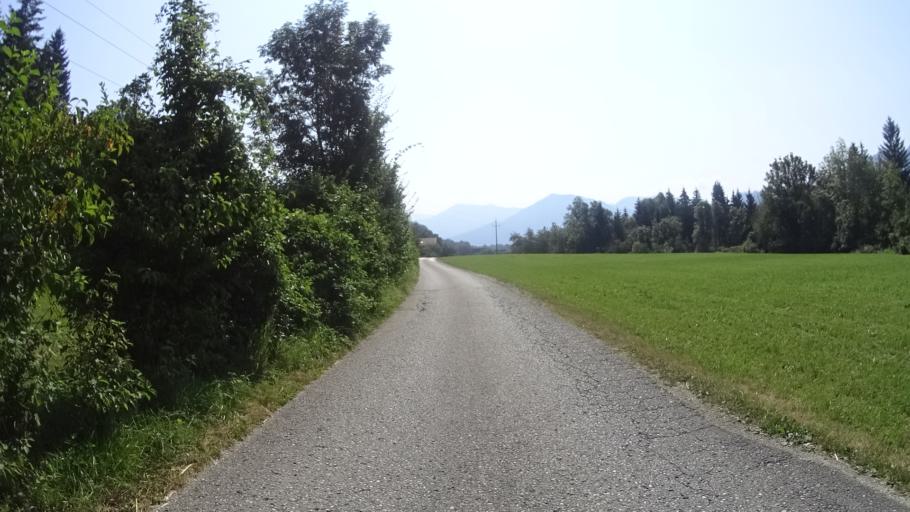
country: AT
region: Carinthia
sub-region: Politischer Bezirk Volkermarkt
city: Gallizien
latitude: 46.5646
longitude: 14.5357
